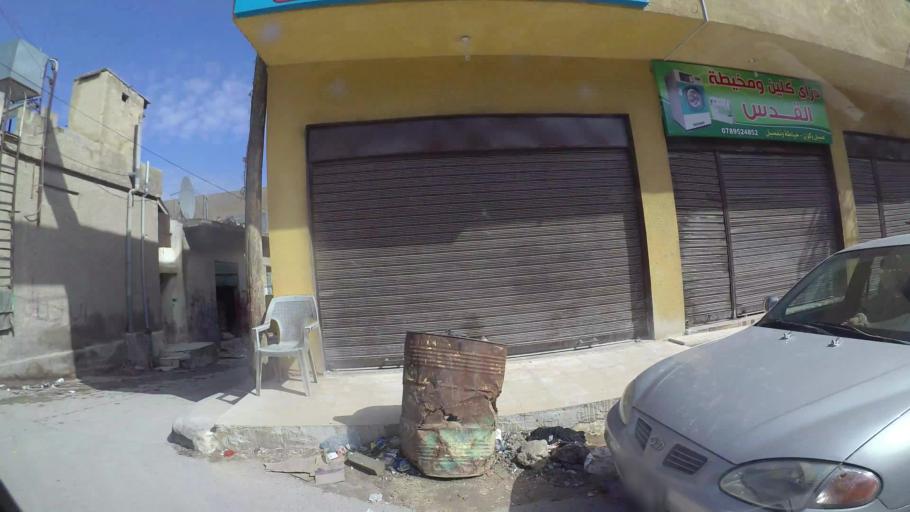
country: JO
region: Amman
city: Al Jubayhah
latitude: 32.0725
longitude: 35.8427
